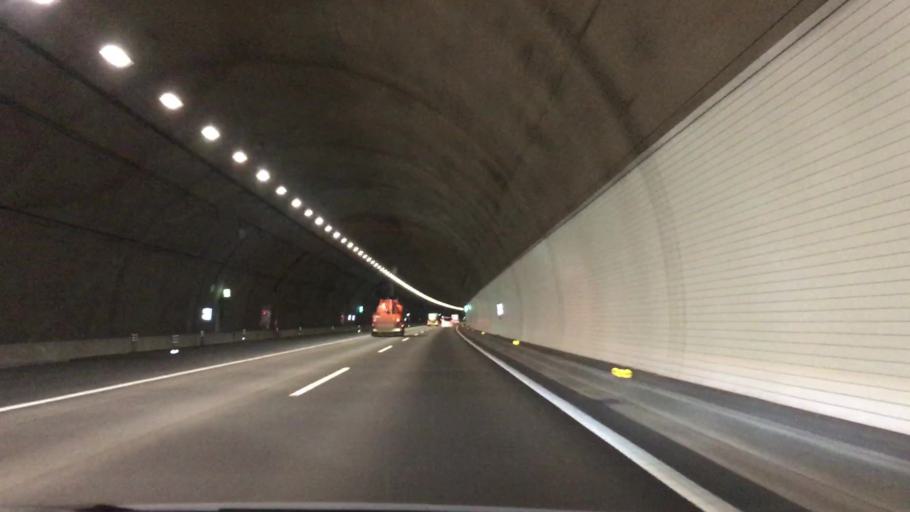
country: JP
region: Shizuoka
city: Hamakita
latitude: 34.8726
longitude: 137.6721
